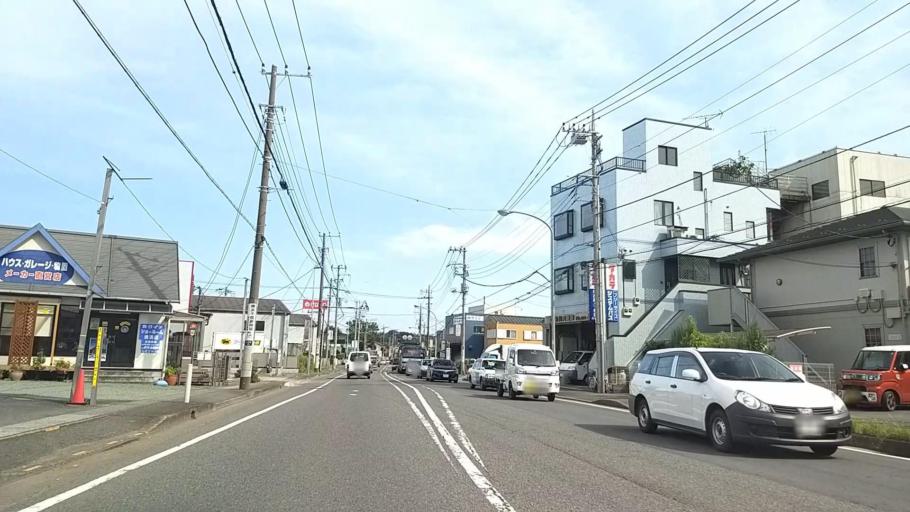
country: JP
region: Kanagawa
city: Yokohama
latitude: 35.5154
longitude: 139.5811
